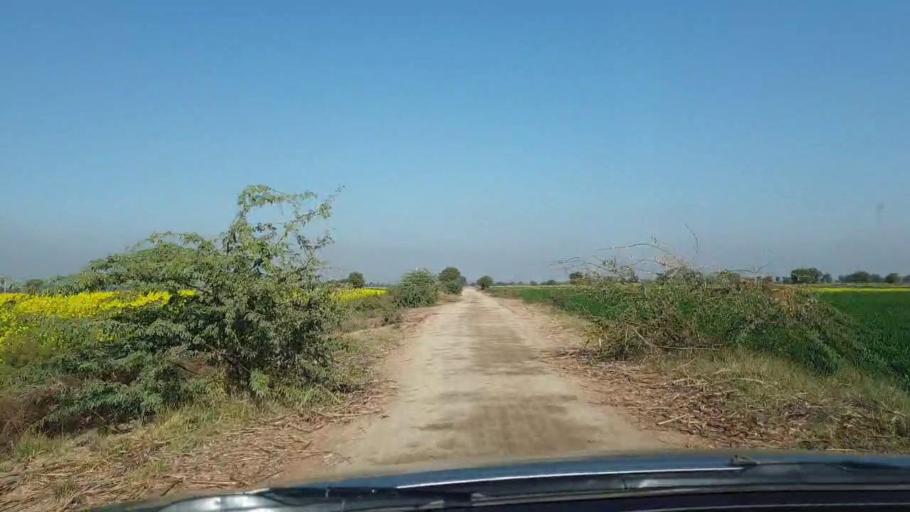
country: PK
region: Sindh
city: Jhol
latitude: 25.8900
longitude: 68.9054
